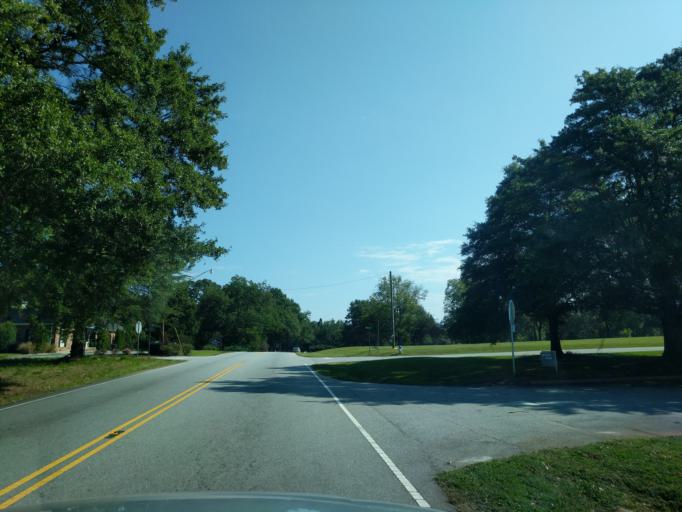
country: US
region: South Carolina
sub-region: Spartanburg County
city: Lyman
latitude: 34.9514
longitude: -82.1224
